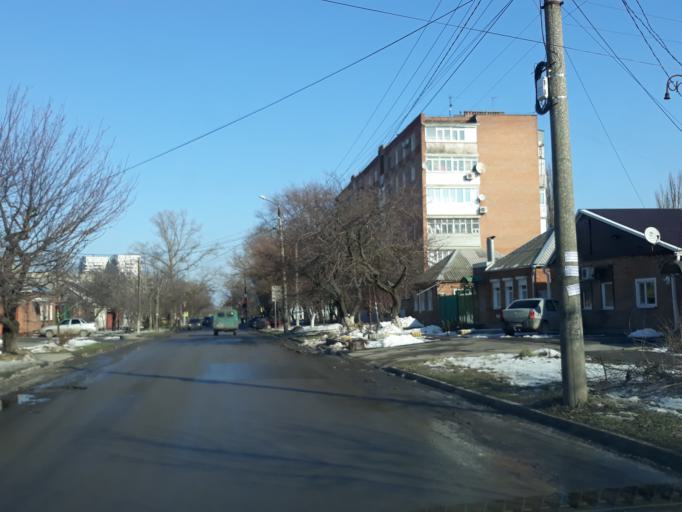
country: RU
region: Rostov
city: Taganrog
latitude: 47.2215
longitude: 38.8759
